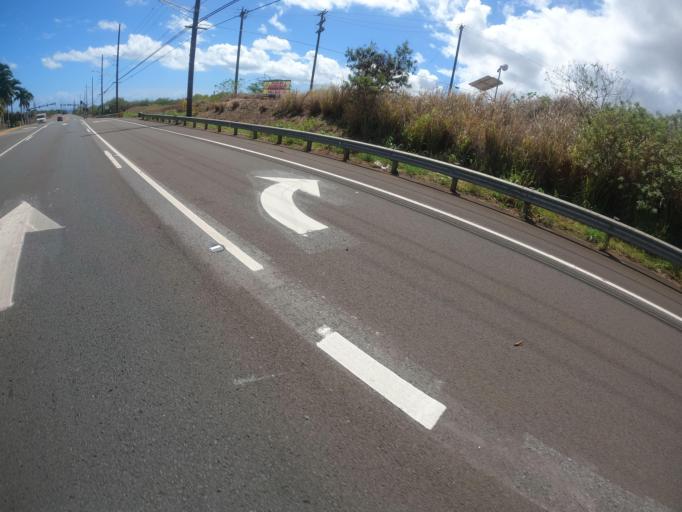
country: US
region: Hawaii
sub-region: Honolulu County
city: Village Park
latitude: 21.3975
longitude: -158.0385
